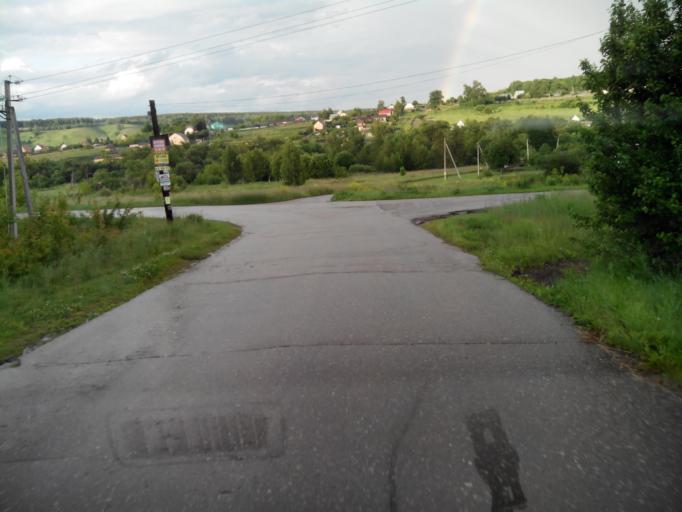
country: RU
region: Penza
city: Zasechnoye
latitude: 53.0688
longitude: 45.0148
